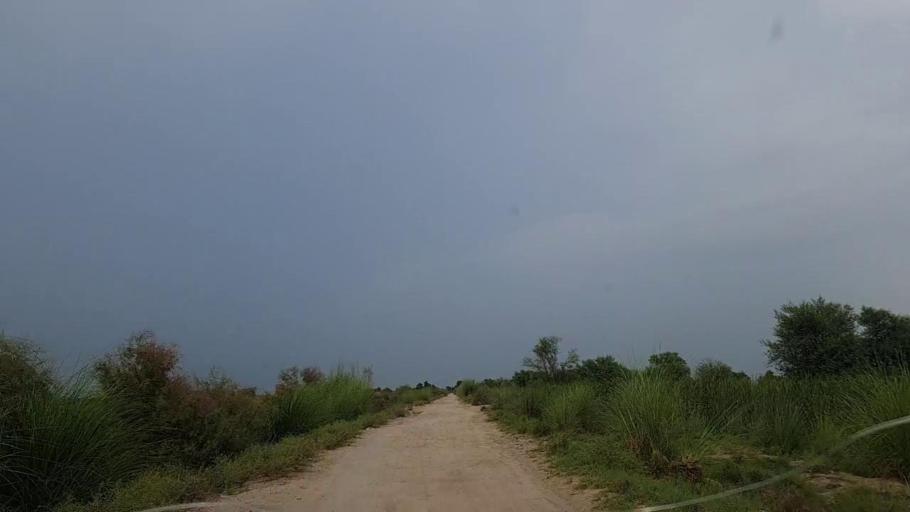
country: PK
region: Sindh
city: Khanpur
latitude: 27.8261
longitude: 69.5580
